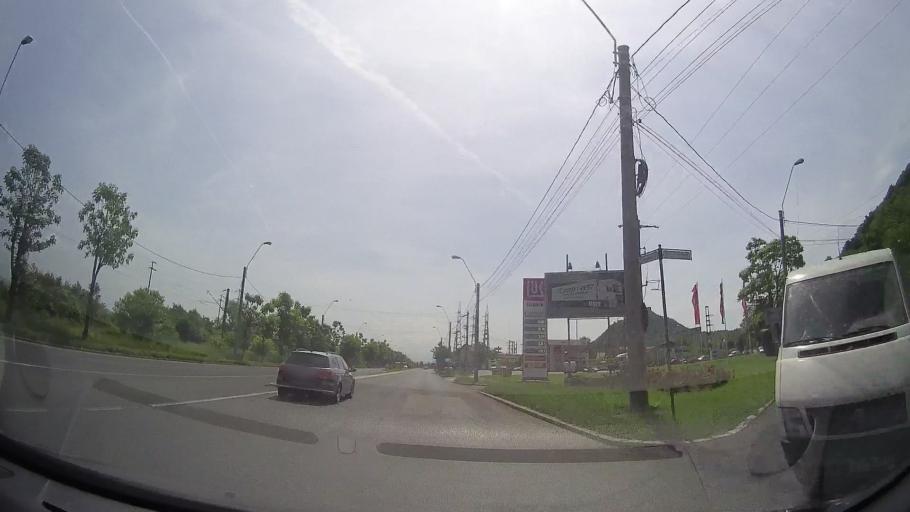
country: RO
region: Hunedoara
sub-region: Comuna Soimus
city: Soimus
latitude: 45.9009
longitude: 22.8873
